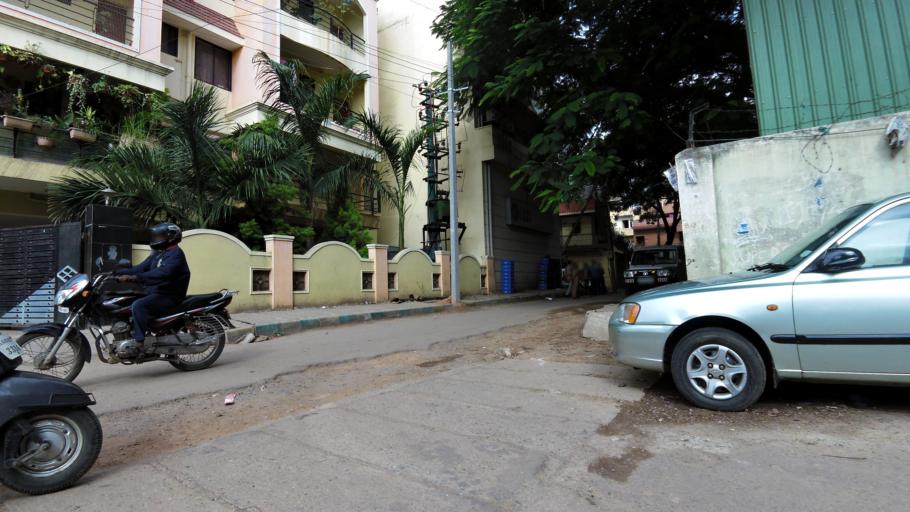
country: IN
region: Karnataka
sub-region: Bangalore Urban
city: Bangalore
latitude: 12.9979
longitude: 77.6290
